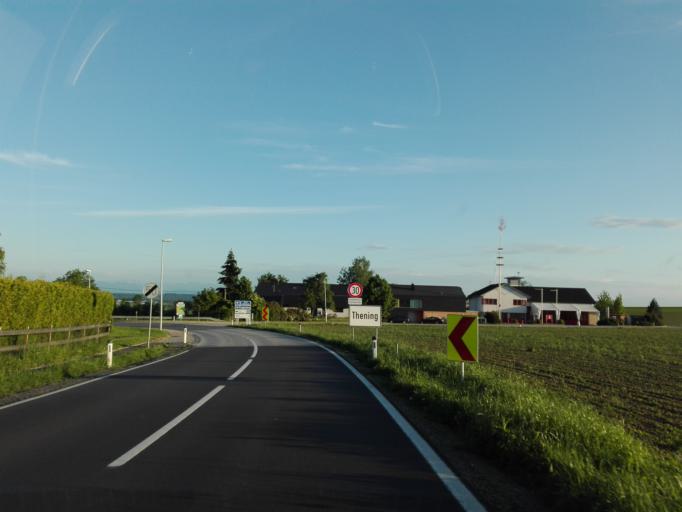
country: AT
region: Upper Austria
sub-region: Politischer Bezirk Linz-Land
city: Horsching
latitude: 48.2579
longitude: 14.1573
